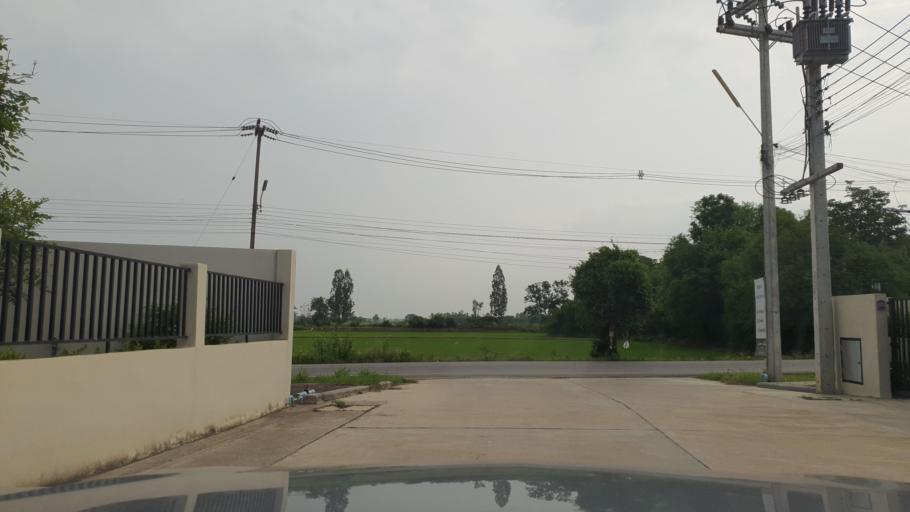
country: TH
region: Phitsanulok
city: Phitsanulok
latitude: 16.8139
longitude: 100.1877
